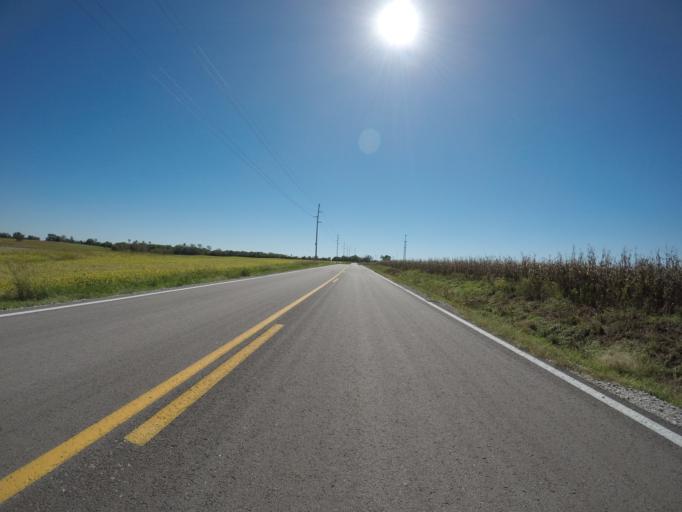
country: US
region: Kansas
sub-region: Johnson County
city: De Soto
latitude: 38.9464
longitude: -95.0195
